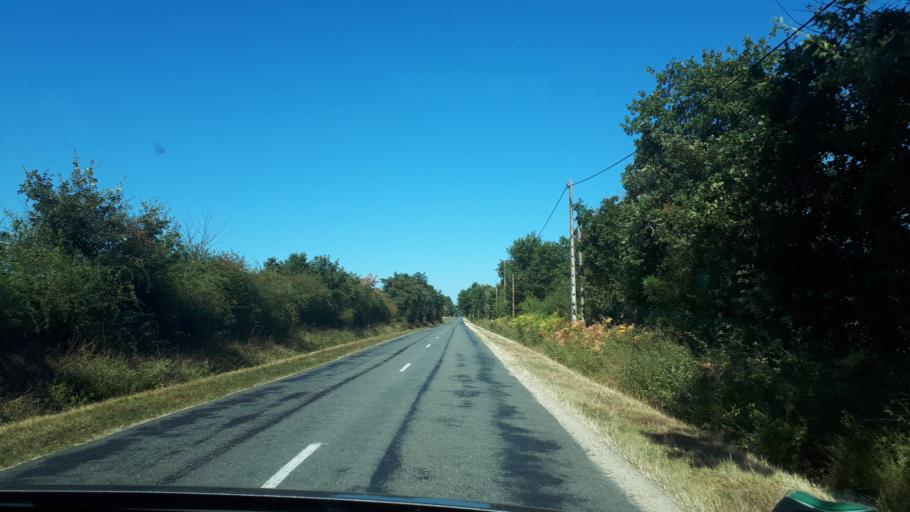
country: FR
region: Centre
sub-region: Departement du Loiret
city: Coullons
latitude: 47.6308
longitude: 2.4698
